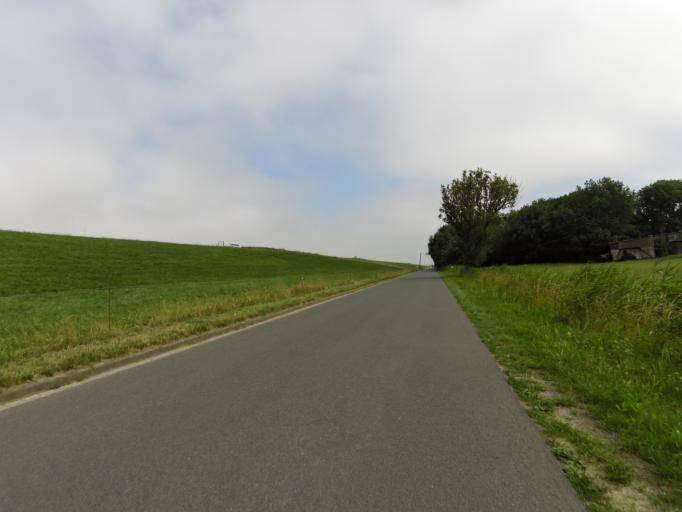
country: DE
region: Lower Saxony
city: Nordholz
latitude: 53.7738
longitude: 8.5472
